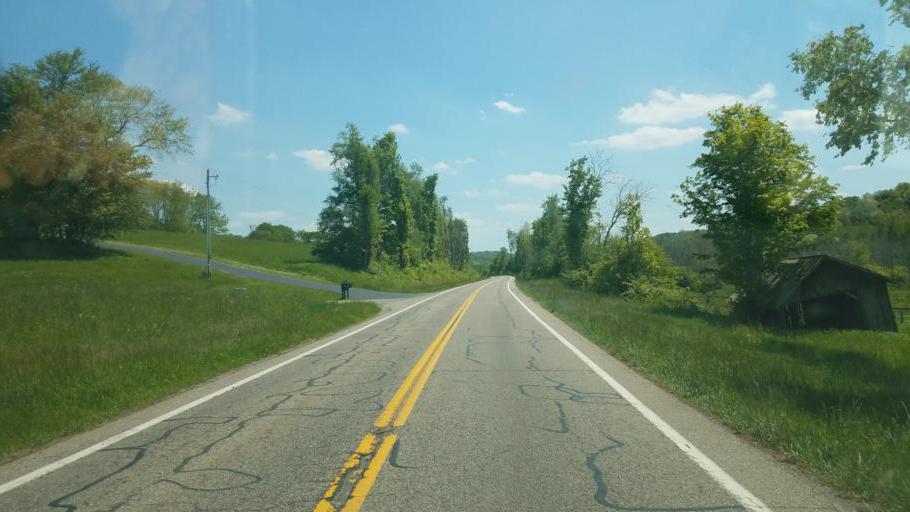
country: US
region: Ohio
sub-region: Muskingum County
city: Frazeysburg
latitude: 40.1732
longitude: -82.2266
